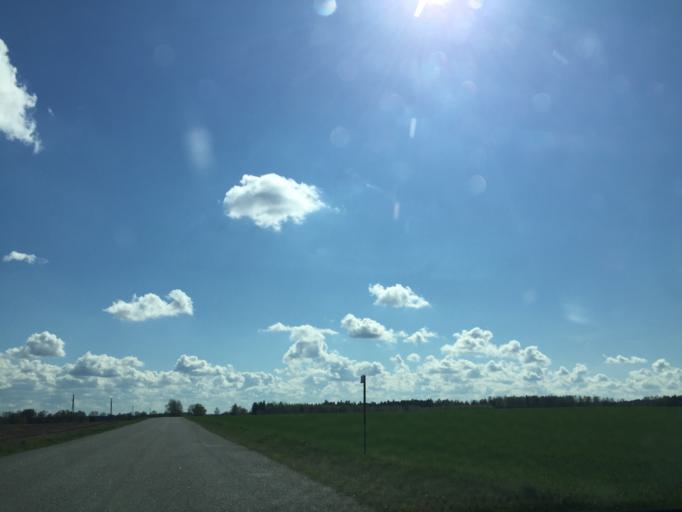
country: LV
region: Strenci
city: Strenci
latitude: 57.5168
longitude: 25.6796
